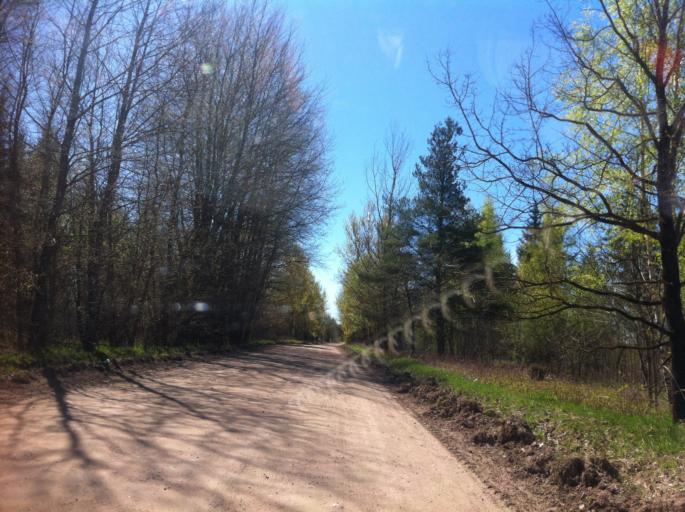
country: RU
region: Pskov
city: Izborsk
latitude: 57.7832
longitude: 27.9626
